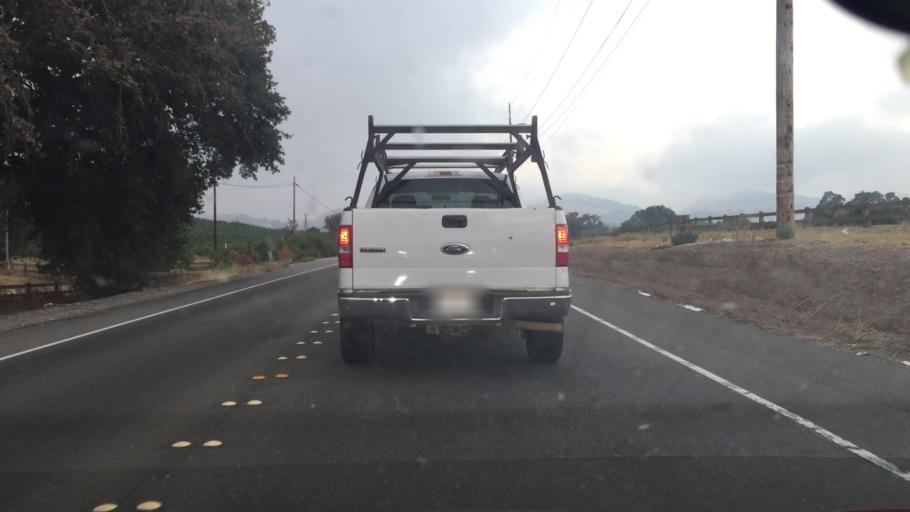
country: US
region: California
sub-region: Alameda County
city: Livermore
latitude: 37.6423
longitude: -121.7927
